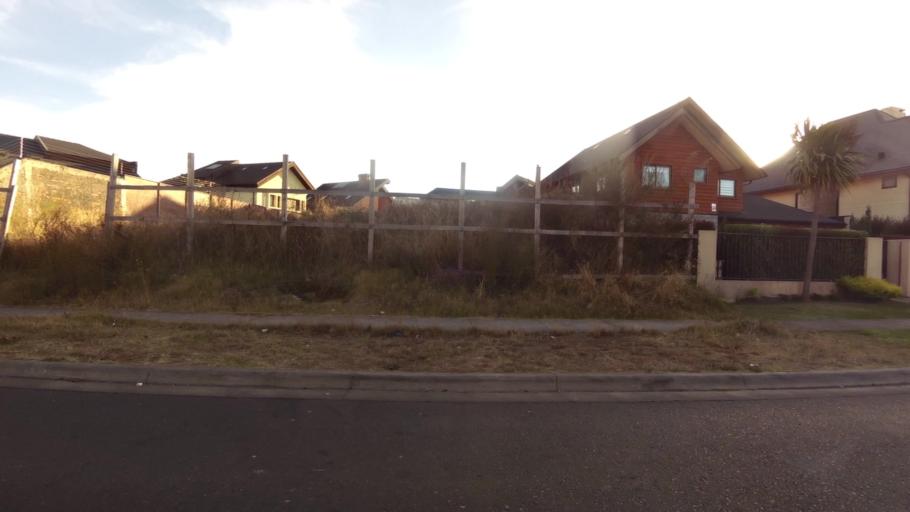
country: CL
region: Biobio
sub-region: Provincia de Concepcion
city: Concepcion
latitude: -36.8599
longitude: -73.0999
